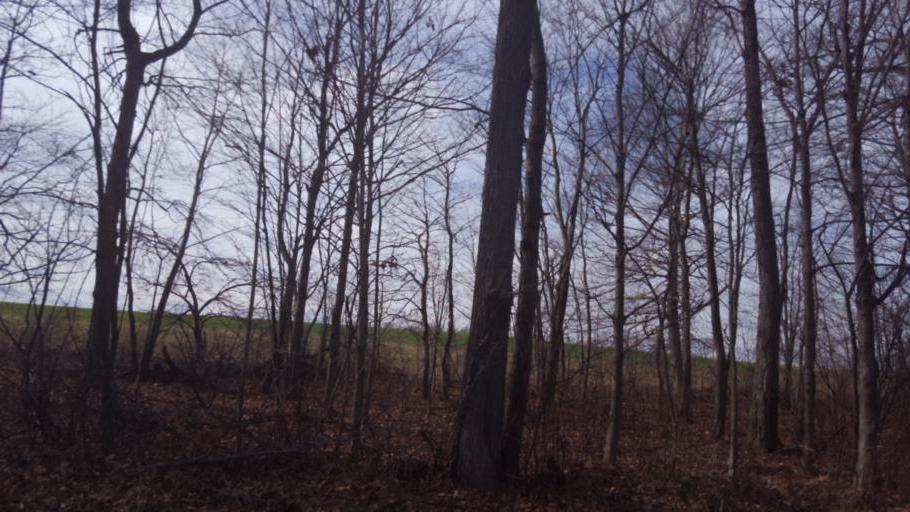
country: US
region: Ohio
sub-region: Sandusky County
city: Bellville
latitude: 40.5469
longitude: -82.4070
